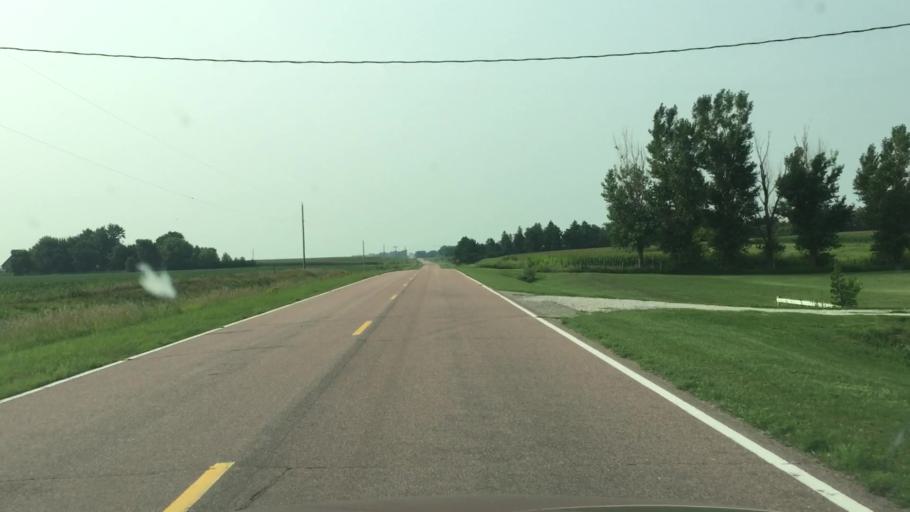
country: US
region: Iowa
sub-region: O'Brien County
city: Sheldon
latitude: 43.2487
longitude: -95.7833
